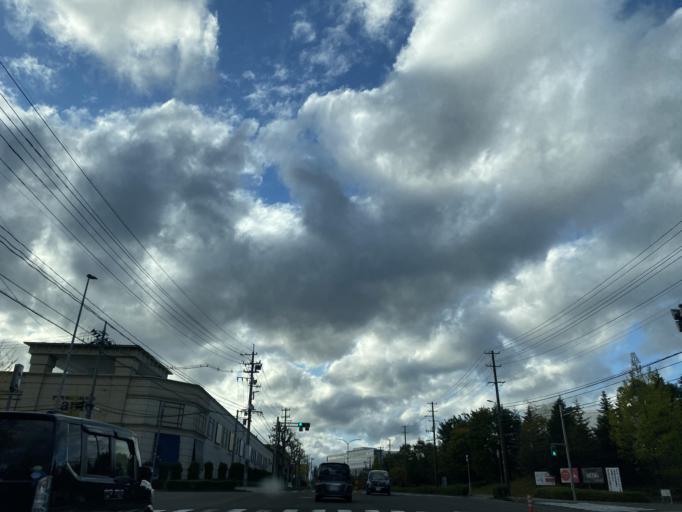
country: JP
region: Miyagi
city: Tomiya
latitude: 38.3438
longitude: 140.8377
